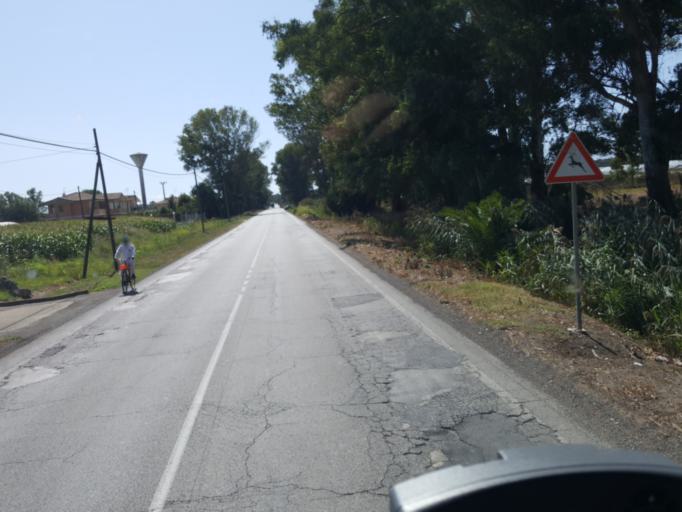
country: IT
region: Latium
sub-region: Provincia di Latina
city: Sabaudia
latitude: 41.3476
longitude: 13.0929
